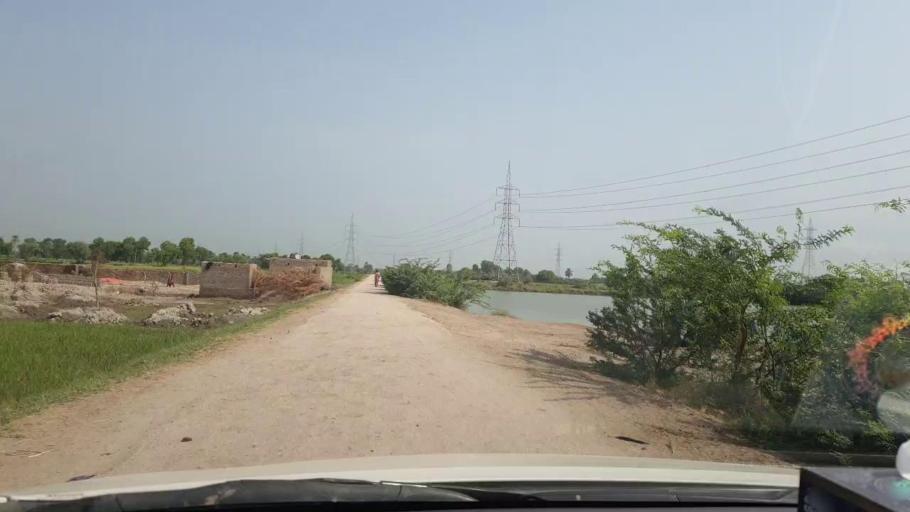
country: PK
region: Sindh
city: Shikarpur
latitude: 27.9744
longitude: 68.6649
